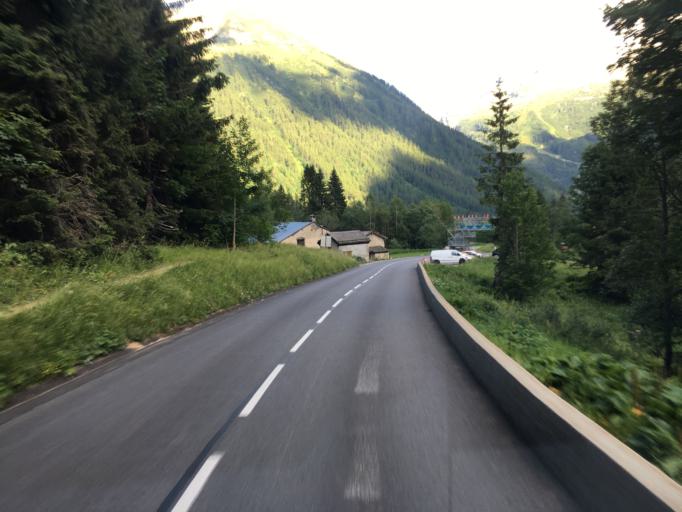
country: FR
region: Rhone-Alpes
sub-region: Departement de la Haute-Savoie
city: Chamonix-Mont-Blanc
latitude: 45.9982
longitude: 6.9250
